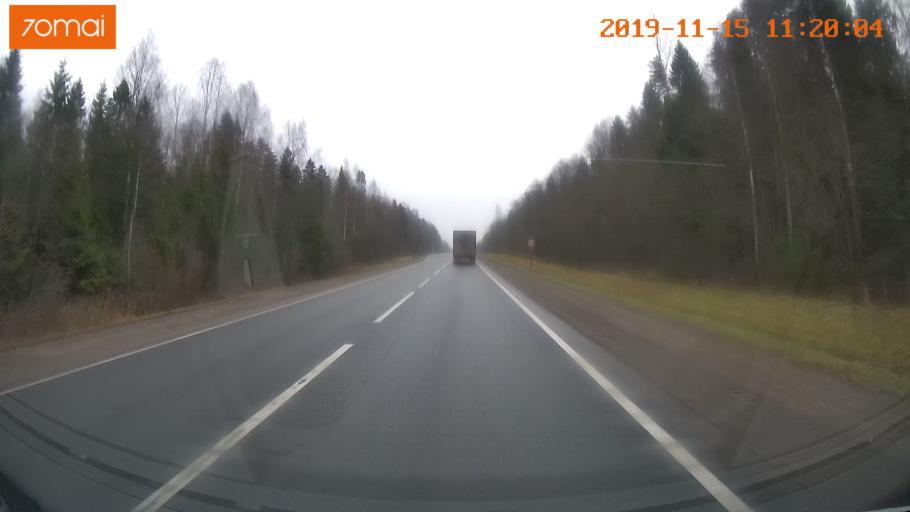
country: RU
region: Vologda
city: Molochnoye
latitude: 59.1405
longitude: 39.3071
